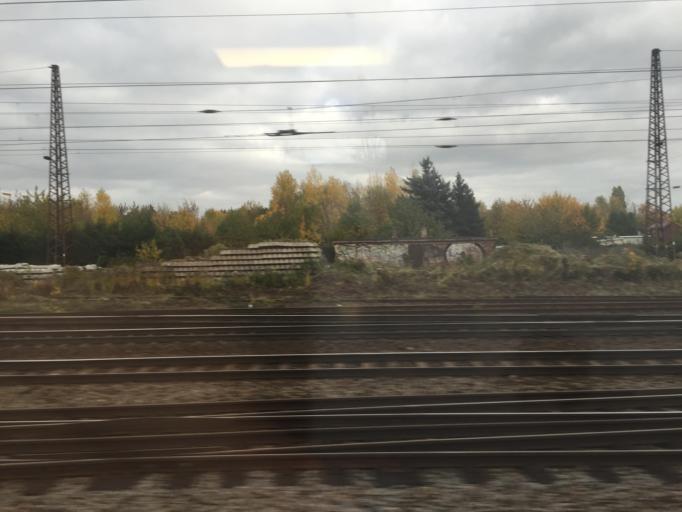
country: DE
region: Saxony
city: Leipzig
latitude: 51.3777
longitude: 12.3966
